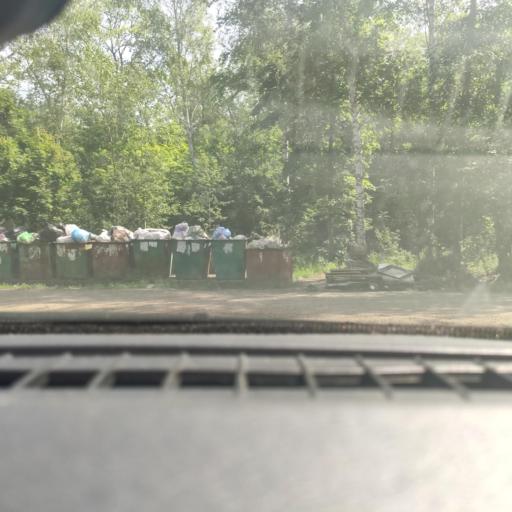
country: RU
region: Voronezj
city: Podgornoye
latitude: 51.8497
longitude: 39.2105
